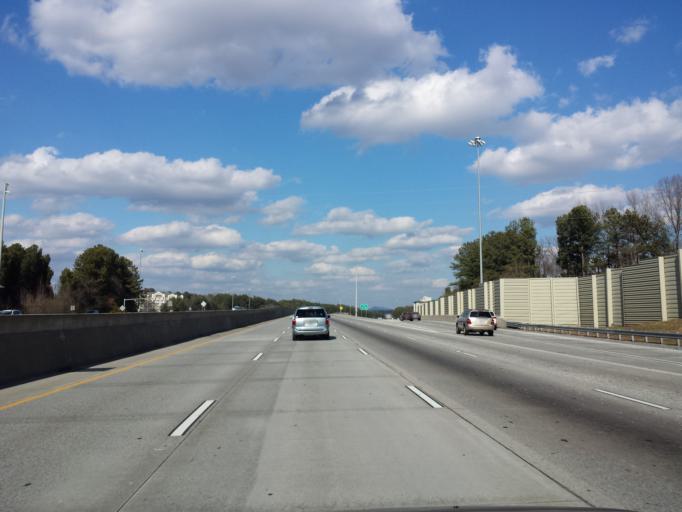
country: US
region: Georgia
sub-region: Fulton County
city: Alpharetta
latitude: 34.0838
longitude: -84.2640
